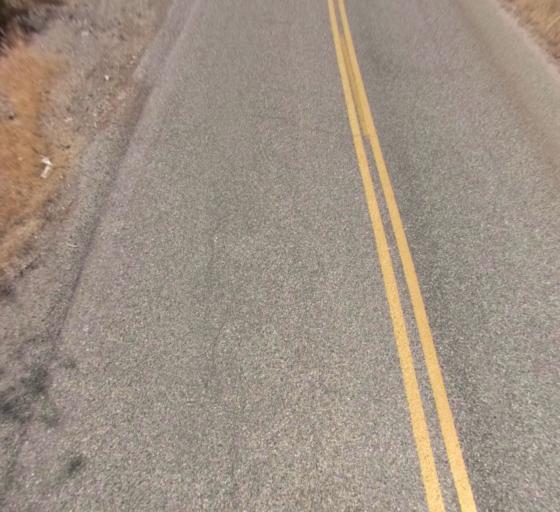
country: US
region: California
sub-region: Fresno County
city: Auberry
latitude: 37.2194
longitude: -119.3518
